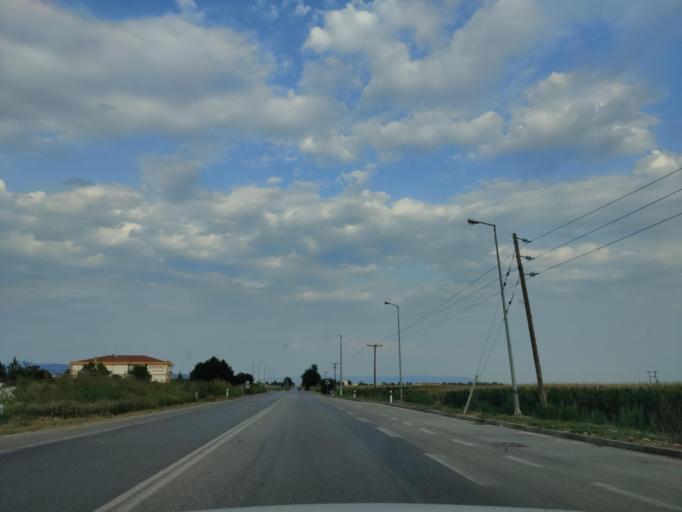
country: GR
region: East Macedonia and Thrace
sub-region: Nomos Dramas
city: Xiropotamos
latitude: 41.1653
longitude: 24.0600
